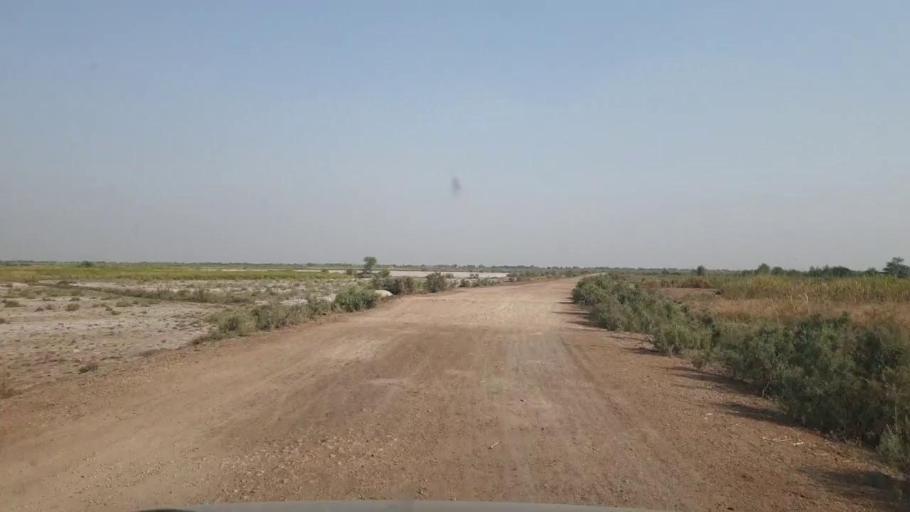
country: PK
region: Sindh
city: Sanghar
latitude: 26.0576
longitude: 68.8937
